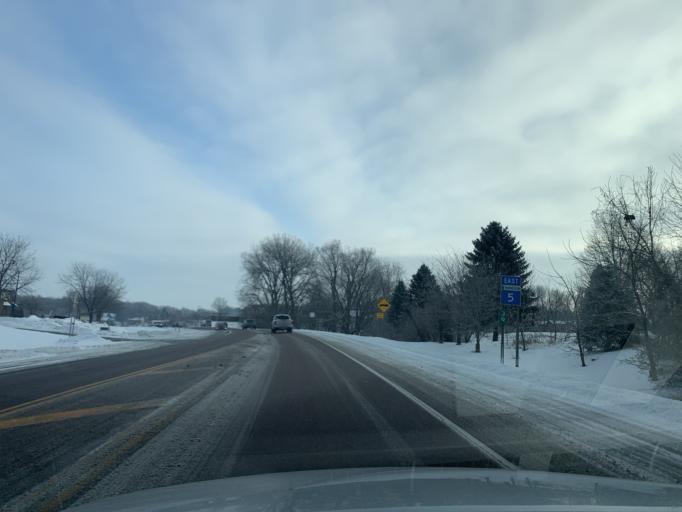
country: US
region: Minnesota
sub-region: Carver County
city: Victoria
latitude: 44.8587
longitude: -93.6597
